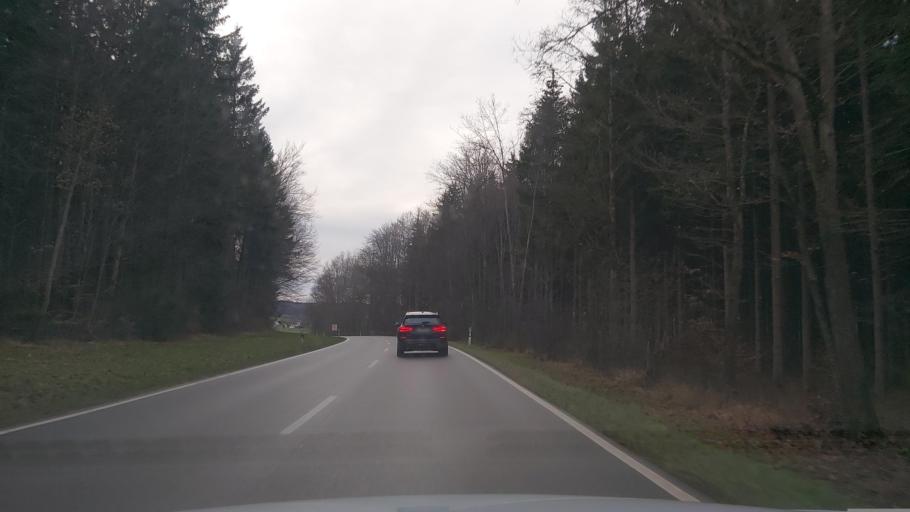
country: DE
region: Baden-Wuerttemberg
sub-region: Tuebingen Region
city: Allmendingen
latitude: 48.3073
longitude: 9.6649
